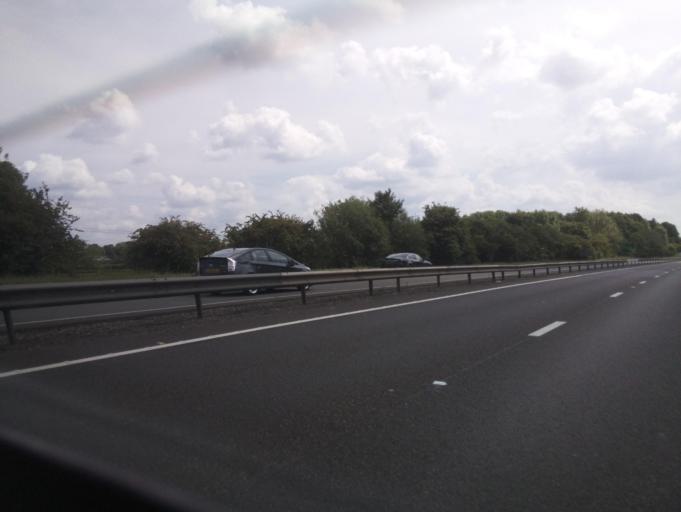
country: GB
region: England
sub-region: North Yorkshire
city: Thirsk
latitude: 54.2367
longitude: -1.3272
